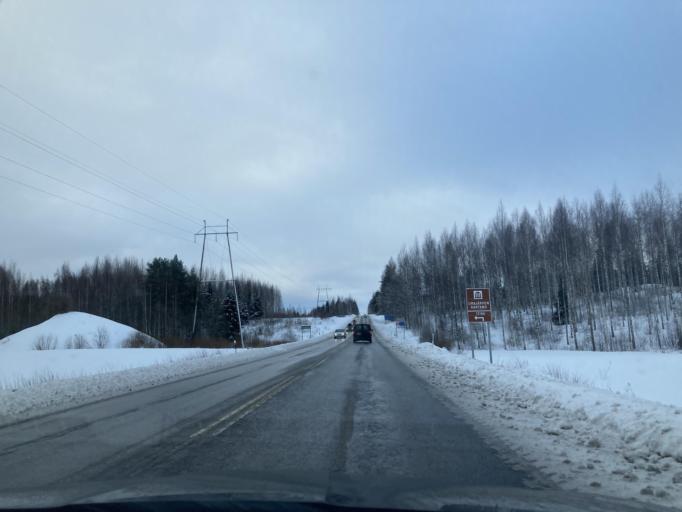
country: FI
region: Paijanne Tavastia
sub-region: Lahti
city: Lahti
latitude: 61.1127
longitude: 25.6416
